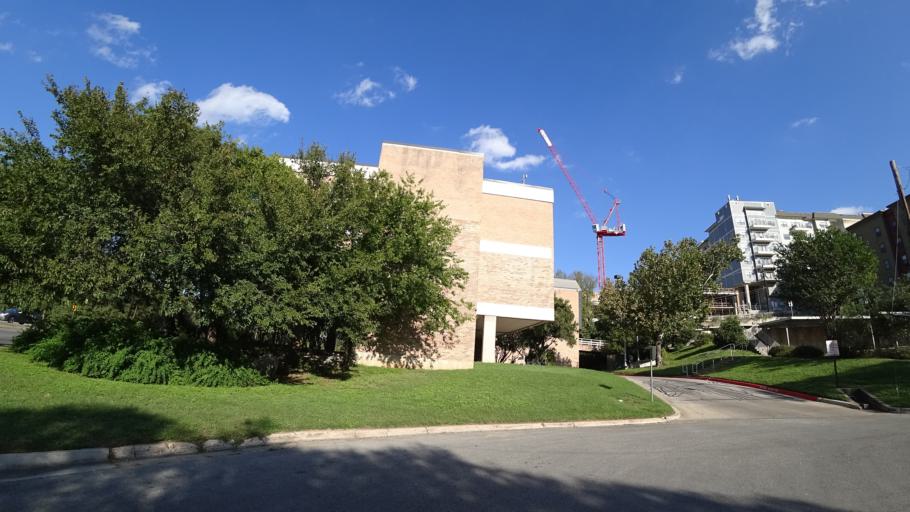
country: US
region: Texas
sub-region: Travis County
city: Austin
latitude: 30.2913
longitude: -97.7506
